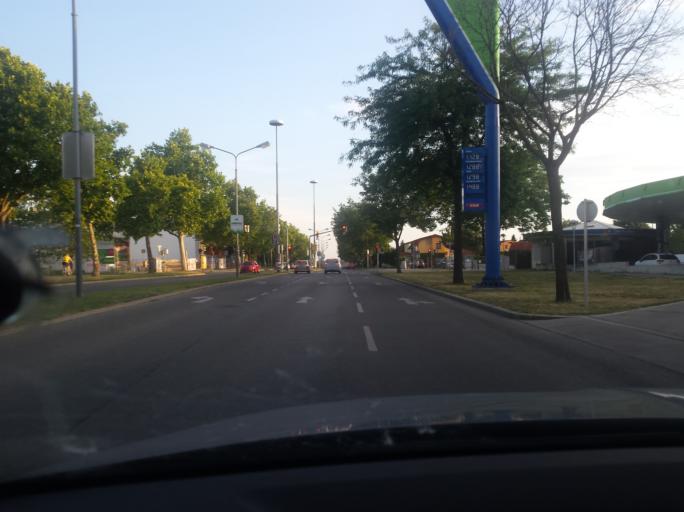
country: AT
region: Lower Austria
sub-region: Politischer Bezirk Wien-Umgebung
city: Schwechat
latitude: 48.1516
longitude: 16.4640
